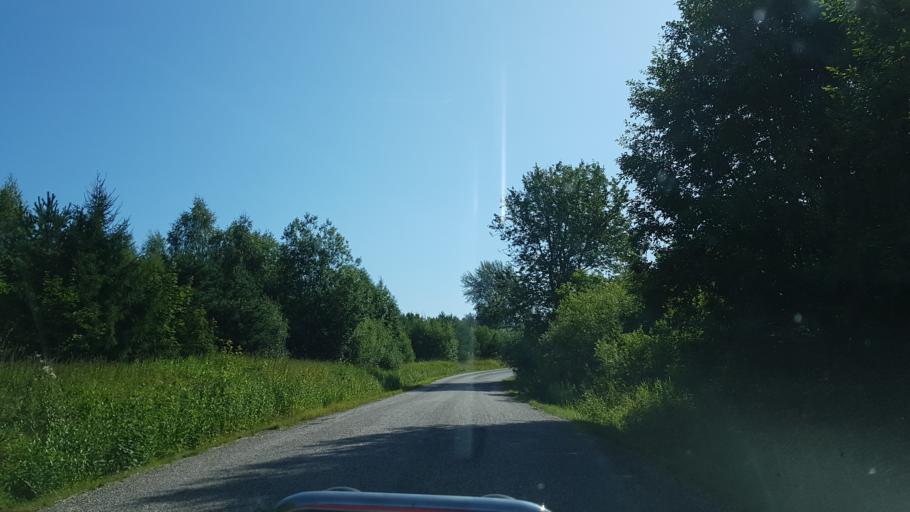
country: EE
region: Vorumaa
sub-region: Voru linn
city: Voru
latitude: 57.7077
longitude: 27.1841
